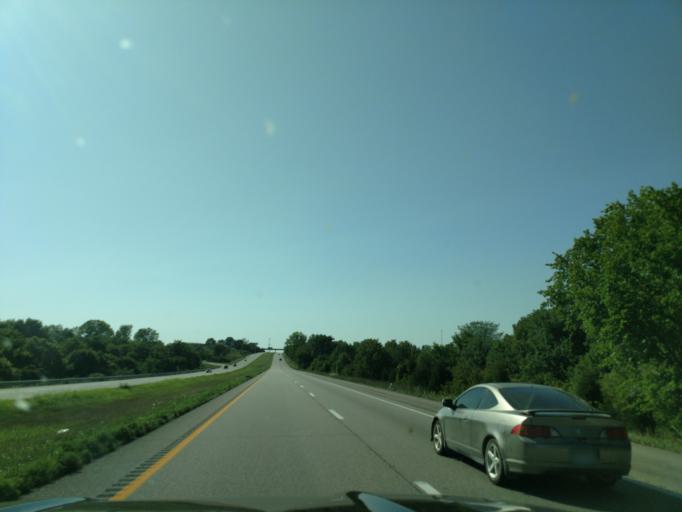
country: US
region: Missouri
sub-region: Andrew County
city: Savannah
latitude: 39.9100
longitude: -94.8948
